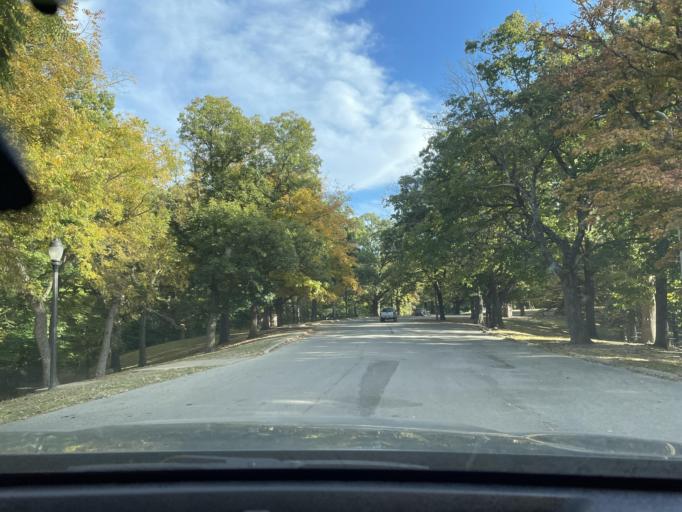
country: US
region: Missouri
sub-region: Buchanan County
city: Saint Joseph
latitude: 39.7992
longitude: -94.8522
